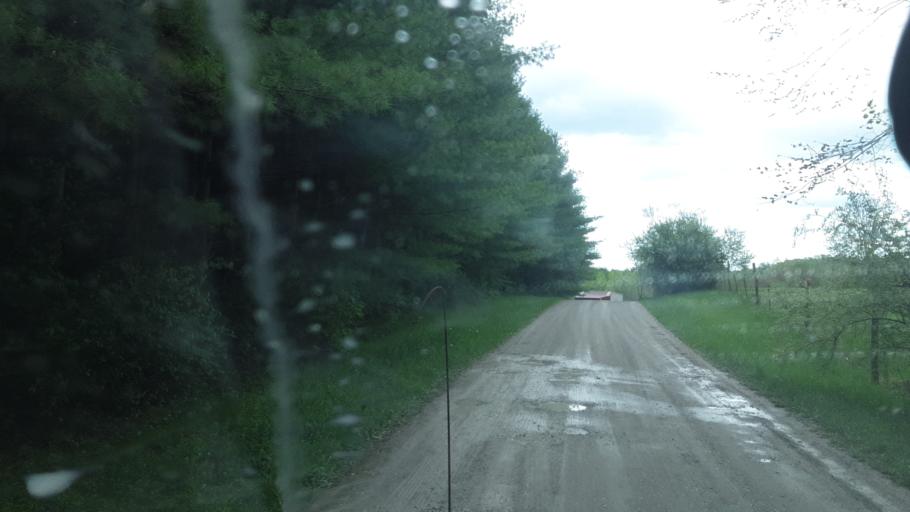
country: US
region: Ohio
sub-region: Noble County
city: Caldwell
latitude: 39.7536
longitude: -81.6198
